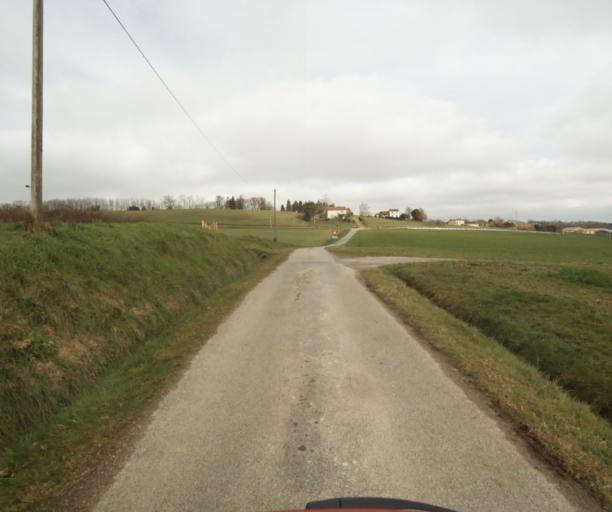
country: FR
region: Midi-Pyrenees
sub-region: Departement de l'Ariege
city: Pamiers
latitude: 43.1088
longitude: 1.5201
